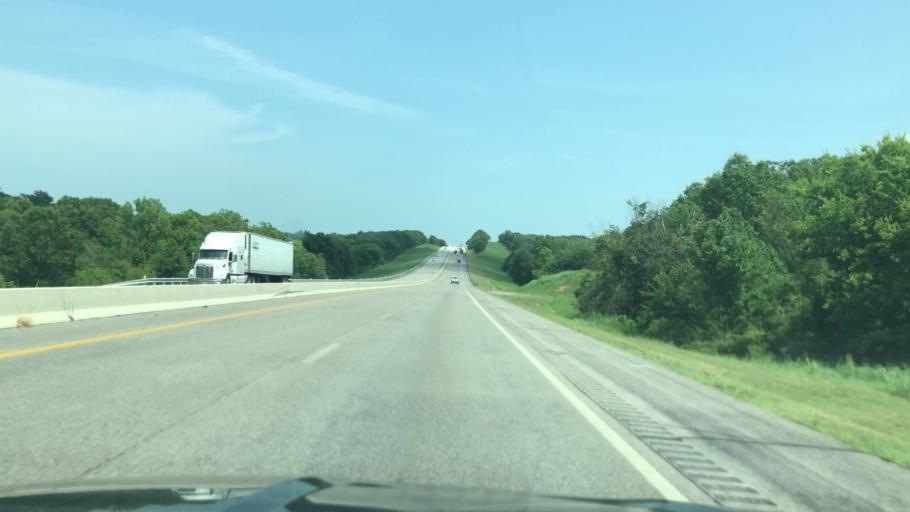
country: US
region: Oklahoma
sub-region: Rogers County
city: Justice
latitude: 36.3385
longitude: -95.5049
